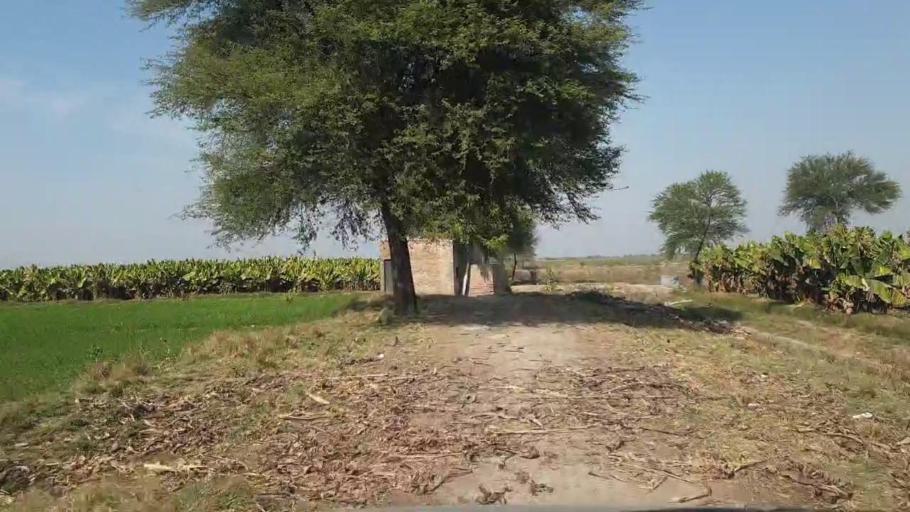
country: PK
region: Sindh
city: Chambar
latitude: 25.3247
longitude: 68.8057
